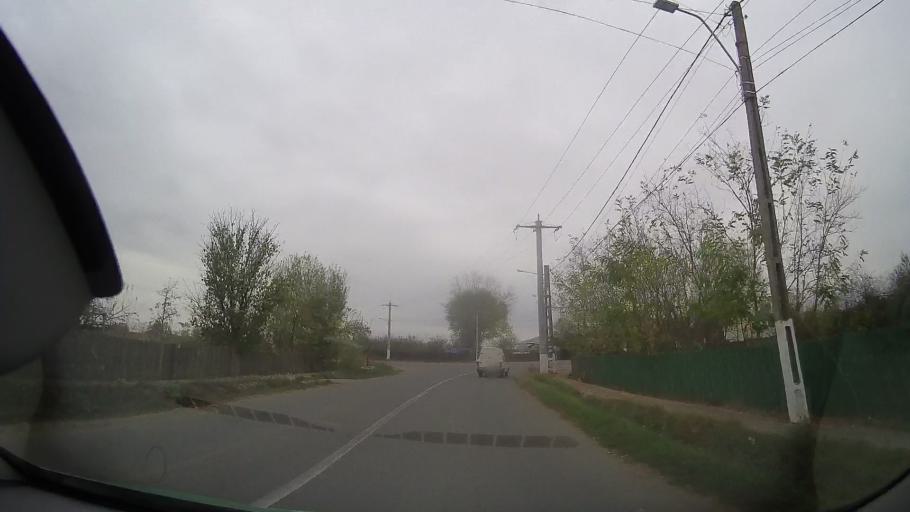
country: RO
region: Braila
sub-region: Comuna Budesti
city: Tataru
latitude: 44.8515
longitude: 27.4239
